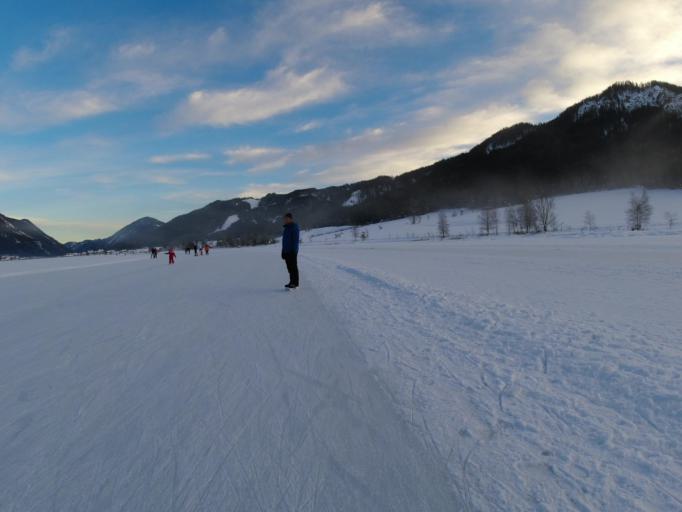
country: AT
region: Carinthia
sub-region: Politischer Bezirk Spittal an der Drau
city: Steinfeld
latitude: 46.7168
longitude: 13.2732
